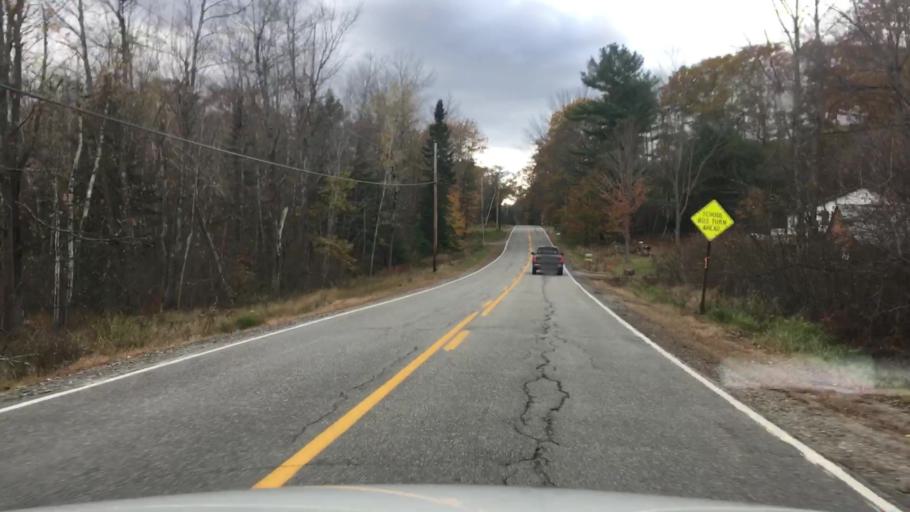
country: US
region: Maine
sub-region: Androscoggin County
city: Sabattus
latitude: 44.1343
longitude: -70.0234
